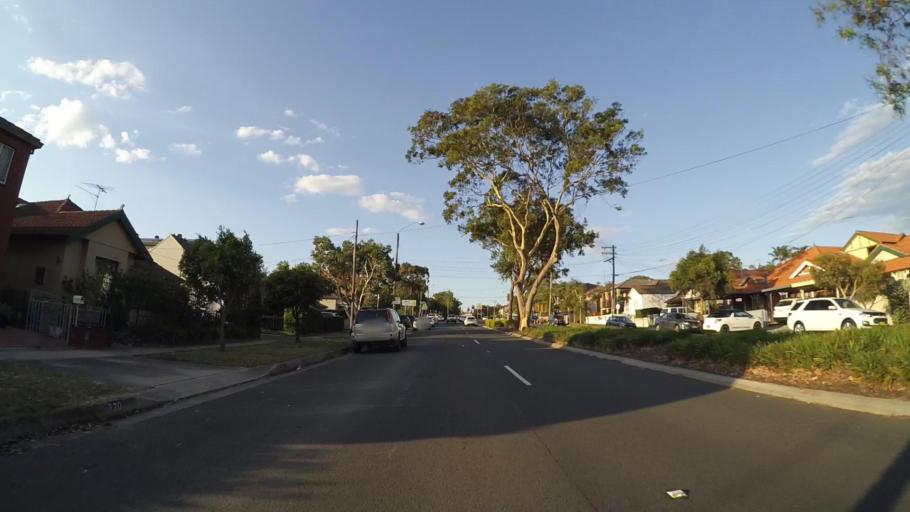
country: AU
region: New South Wales
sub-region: Randwick
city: Daceyville
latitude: -33.9266
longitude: 151.2390
